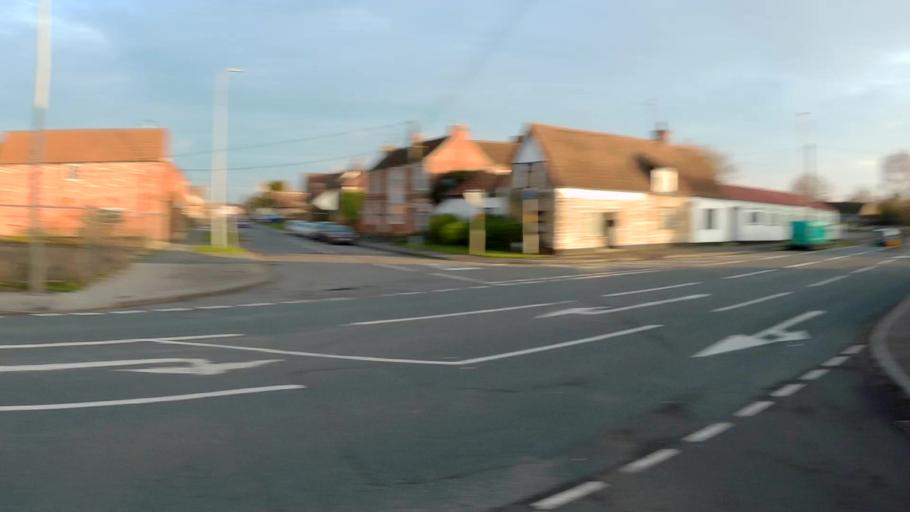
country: GB
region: England
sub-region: Lincolnshire
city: Bourne
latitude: 52.8023
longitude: -0.3803
